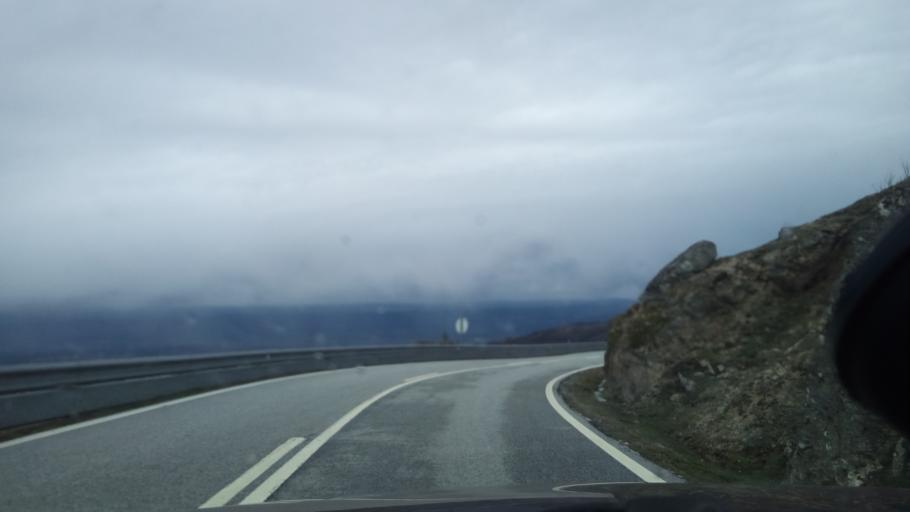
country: PT
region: Guarda
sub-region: Manteigas
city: Manteigas
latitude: 40.4536
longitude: -7.5984
